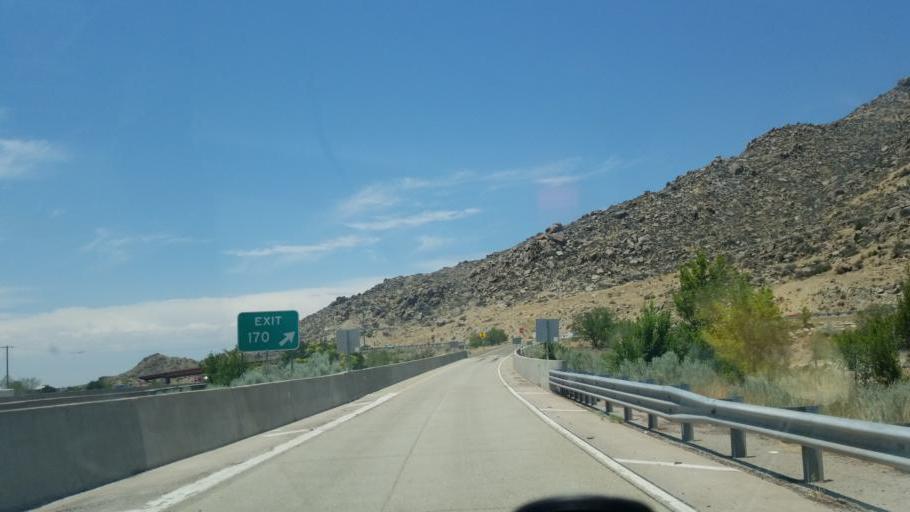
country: US
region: New Mexico
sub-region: Bernalillo County
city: Carnuel
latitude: 35.0622
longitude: -106.4645
